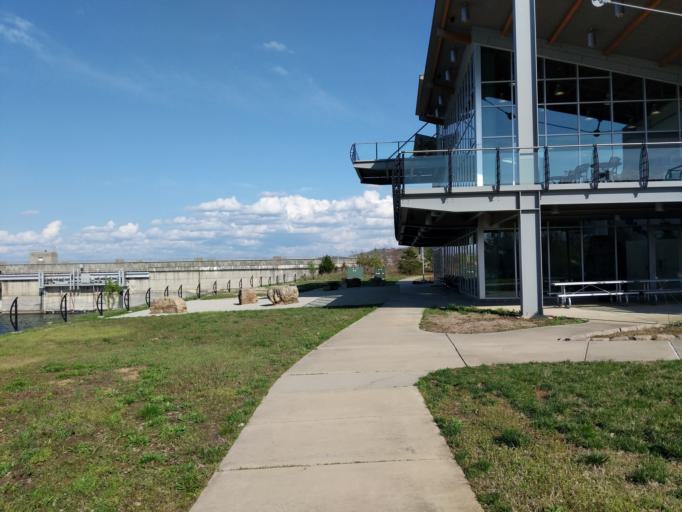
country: US
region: Missouri
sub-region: Taney County
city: Hollister
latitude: 36.5941
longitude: -93.3127
